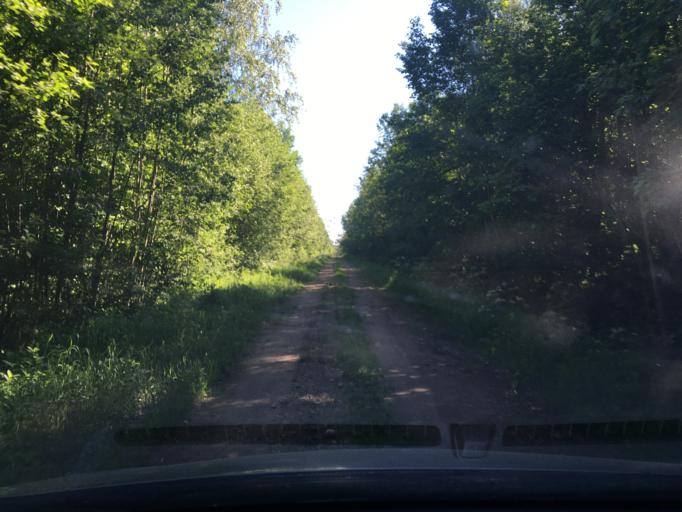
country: EE
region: Laeaene
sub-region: Lihula vald
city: Lihula
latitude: 58.6232
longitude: 23.7126
